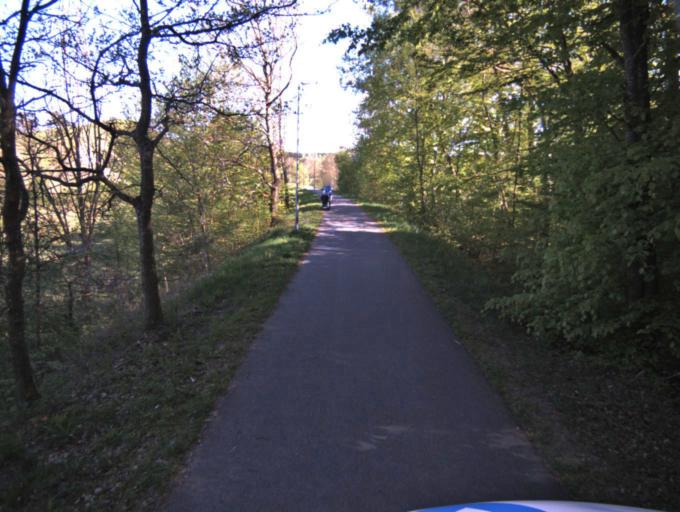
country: SE
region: Skane
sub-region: Kristianstads Kommun
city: Degeberga
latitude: 55.8336
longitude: 14.0802
